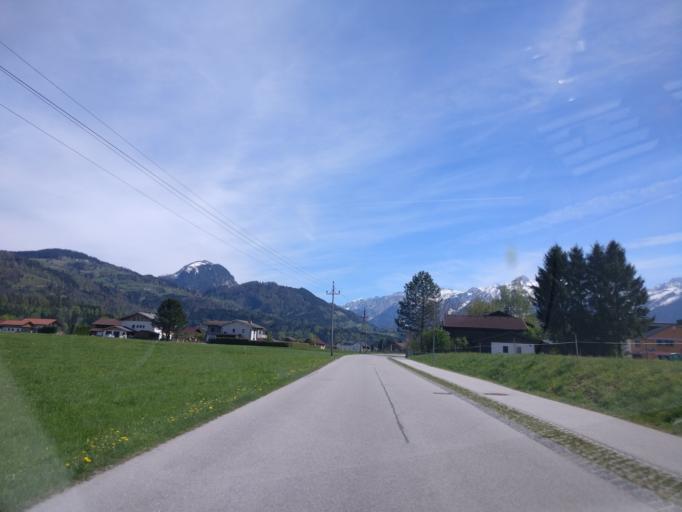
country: AT
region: Salzburg
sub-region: Politischer Bezirk Hallein
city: Kuchl
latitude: 47.6337
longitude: 13.1491
